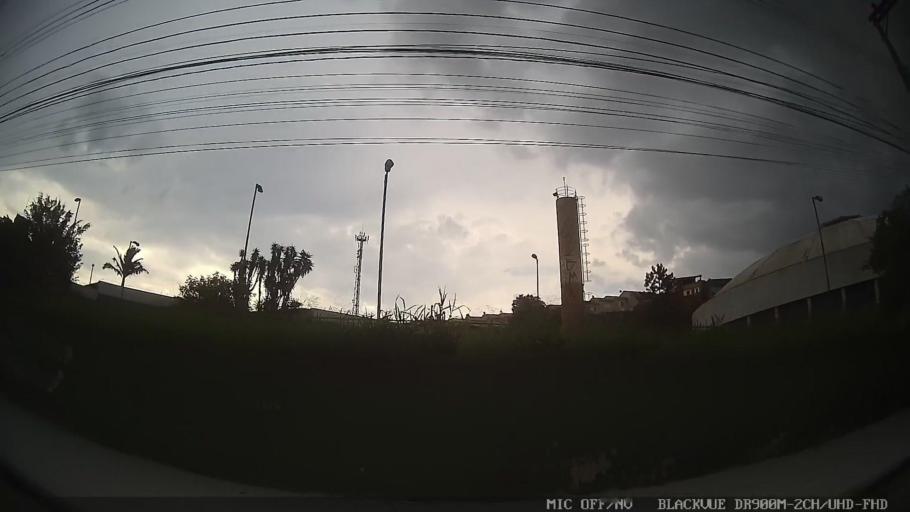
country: BR
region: Sao Paulo
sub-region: Ribeirao Pires
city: Ribeirao Pires
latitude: -23.6763
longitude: -46.4216
